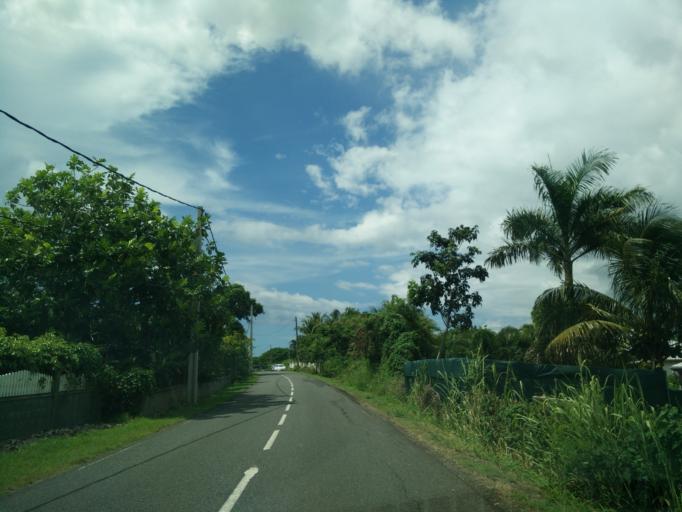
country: GP
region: Guadeloupe
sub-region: Guadeloupe
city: Sainte-Anne
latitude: 16.2630
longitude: -61.3404
